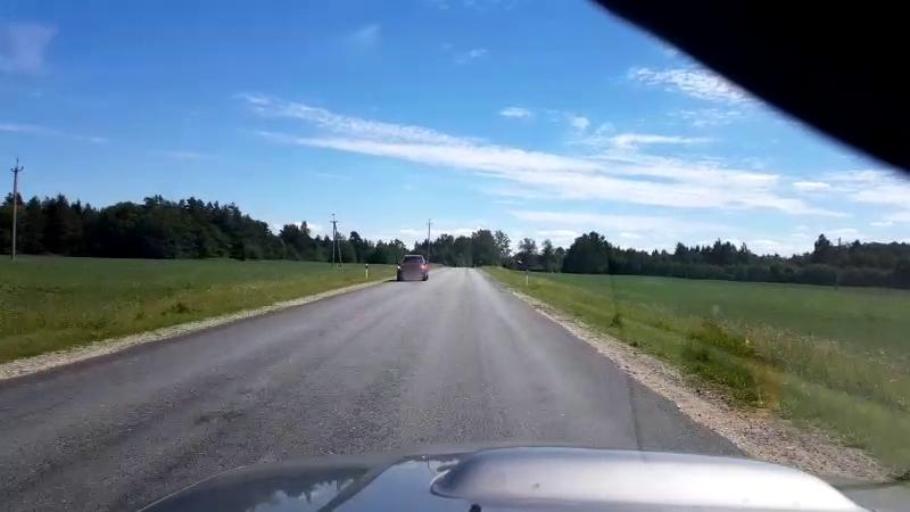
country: EE
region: Laeaene-Virumaa
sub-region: Rakke vald
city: Rakke
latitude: 58.8861
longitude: 26.2891
